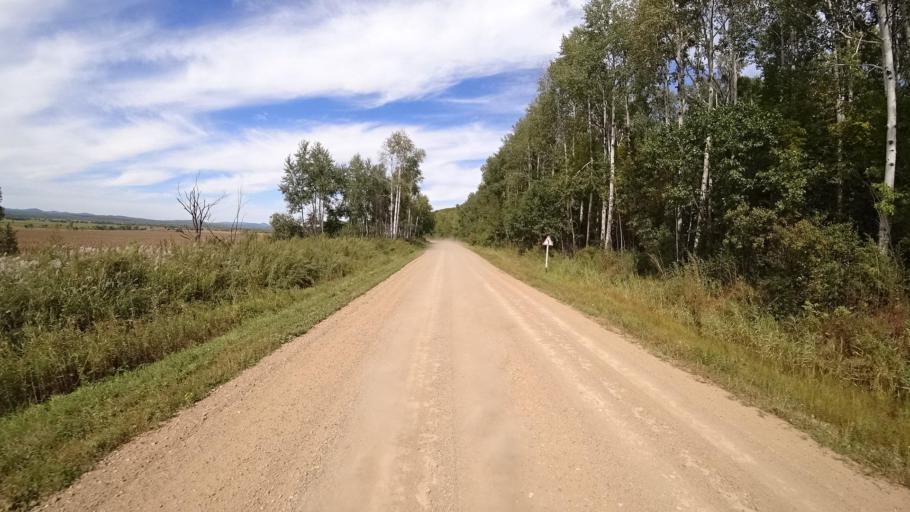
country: RU
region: Primorskiy
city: Yakovlevka
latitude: 44.5671
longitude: 133.5954
